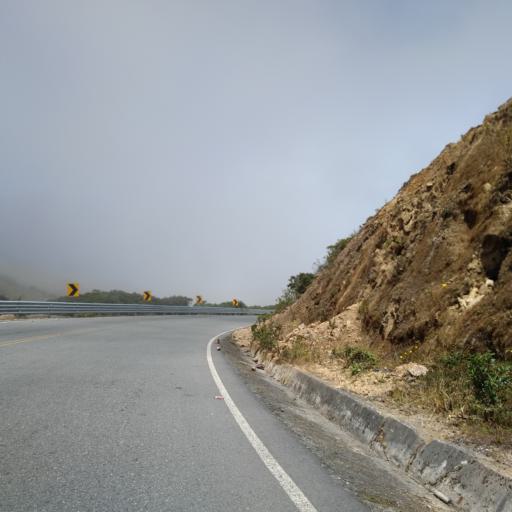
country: EC
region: Cotopaxi
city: La Mana
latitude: -0.9864
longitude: -78.9635
